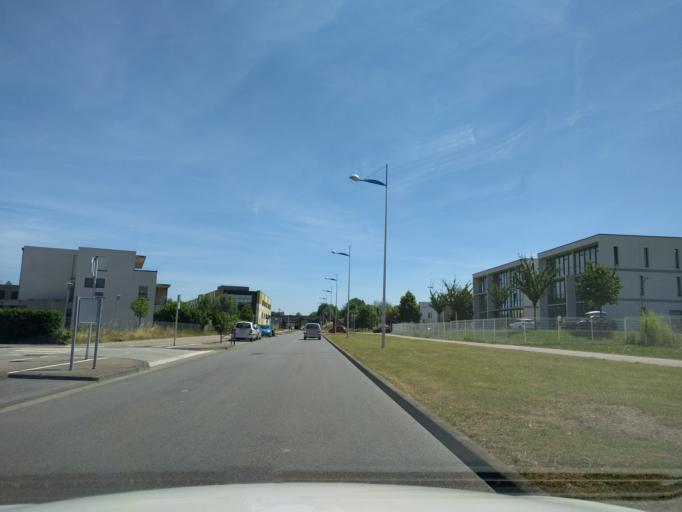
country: FR
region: Lorraine
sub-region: Departement de la Moselle
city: Saint-Julien-les-Metz
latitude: 49.1146
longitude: 6.2313
